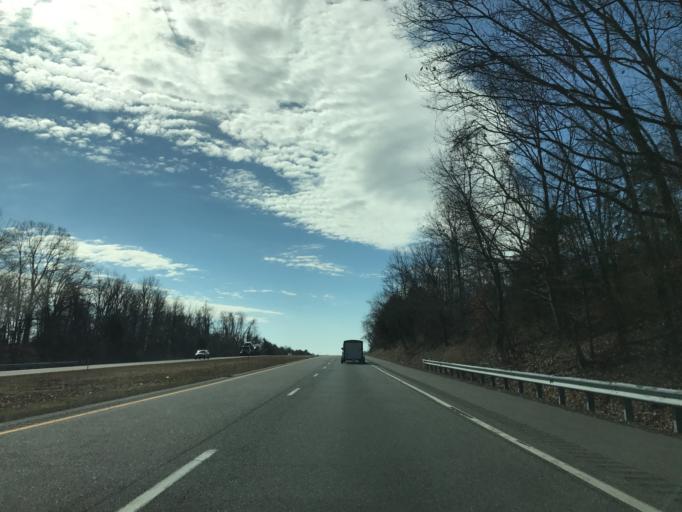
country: US
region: Delaware
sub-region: New Castle County
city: Townsend
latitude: 39.3530
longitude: -75.8230
